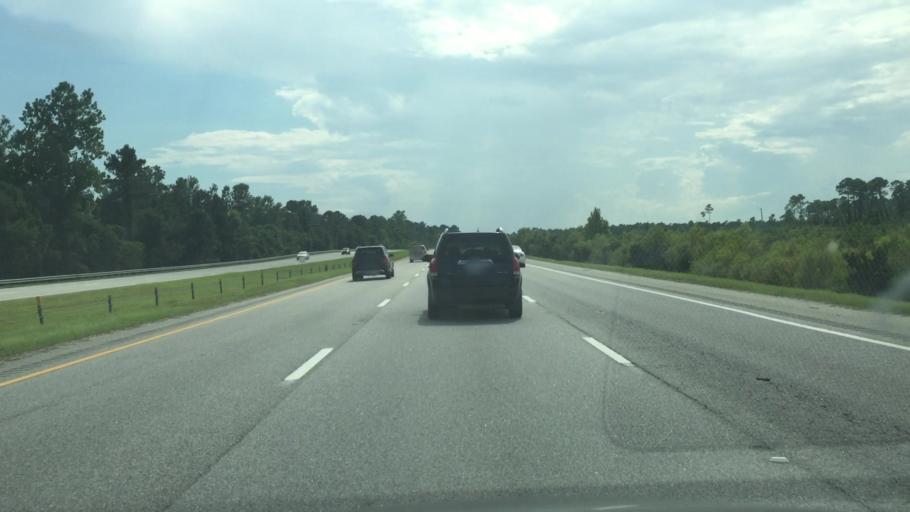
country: US
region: South Carolina
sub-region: Horry County
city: Myrtle Beach
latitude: 33.7731
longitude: -78.8201
